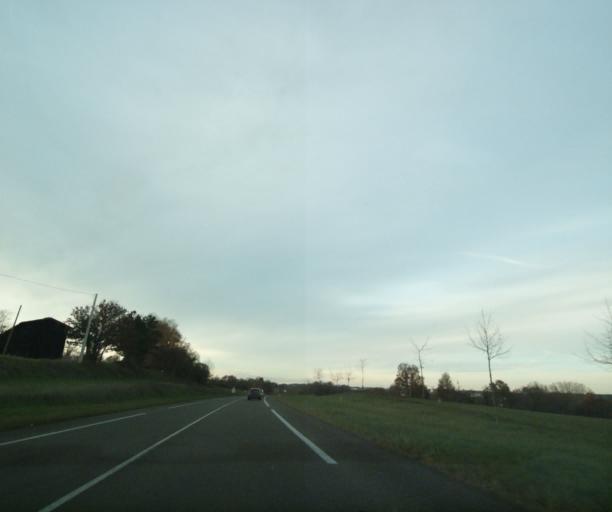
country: FR
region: Aquitaine
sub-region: Departement de la Gironde
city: Bazas
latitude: 44.4234
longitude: -0.2260
